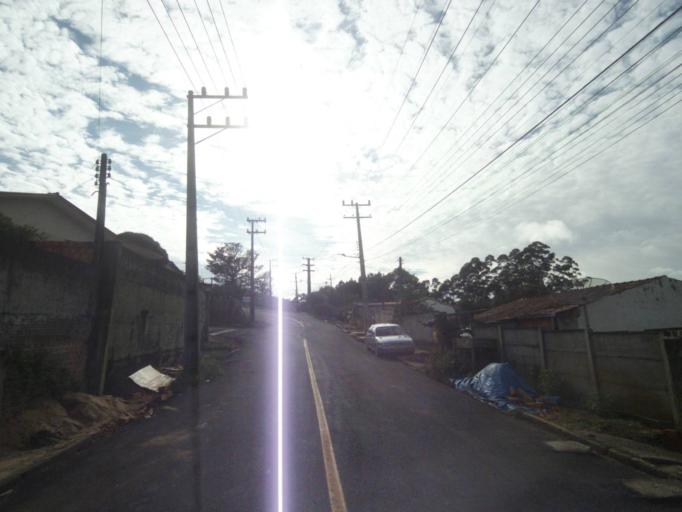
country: BR
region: Parana
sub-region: Telemaco Borba
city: Telemaco Borba
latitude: -24.3405
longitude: -50.6120
